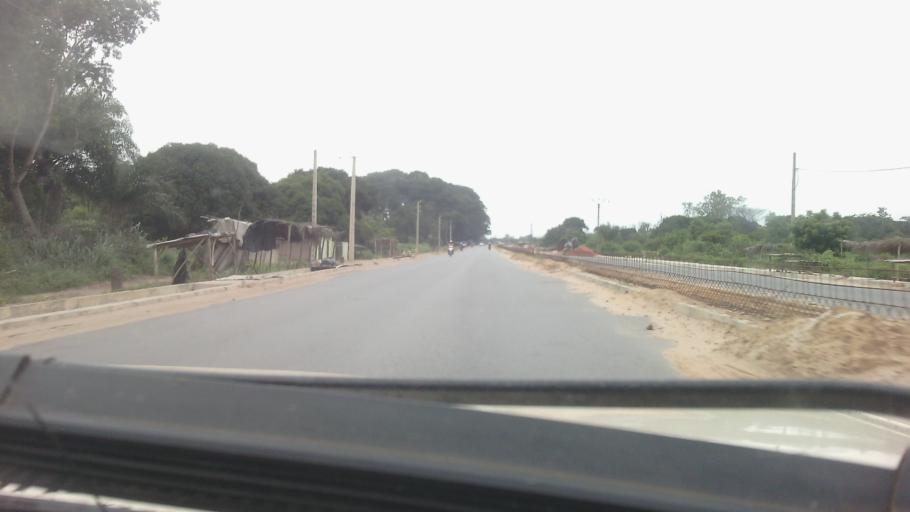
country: BJ
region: Atlantique
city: Ouidah
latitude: 6.3701
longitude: 2.1346
